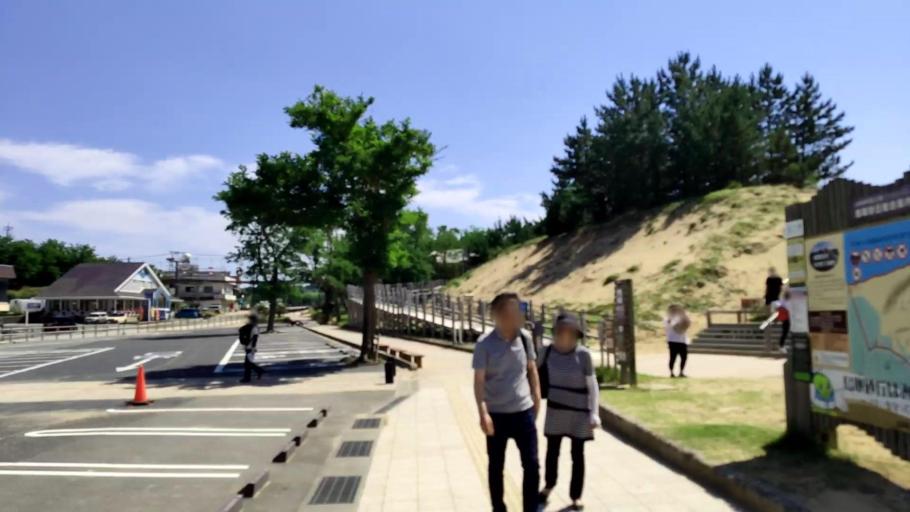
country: JP
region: Tottori
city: Tottori
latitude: 35.5437
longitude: 134.2367
